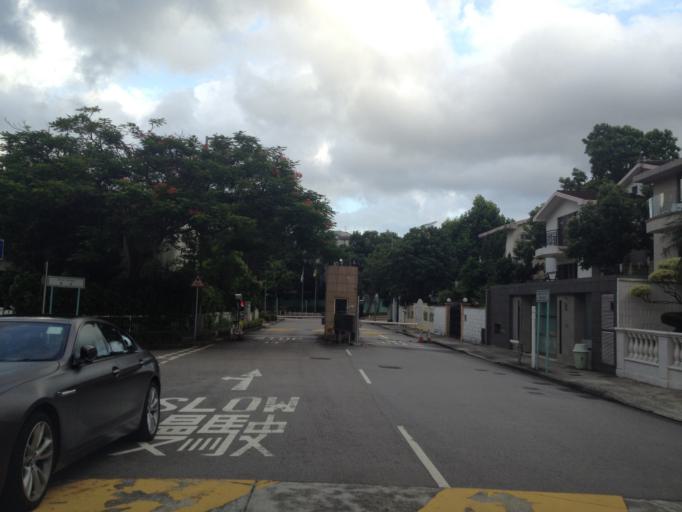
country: HK
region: Tai Po
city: Tai Po
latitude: 22.4608
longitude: 114.1521
